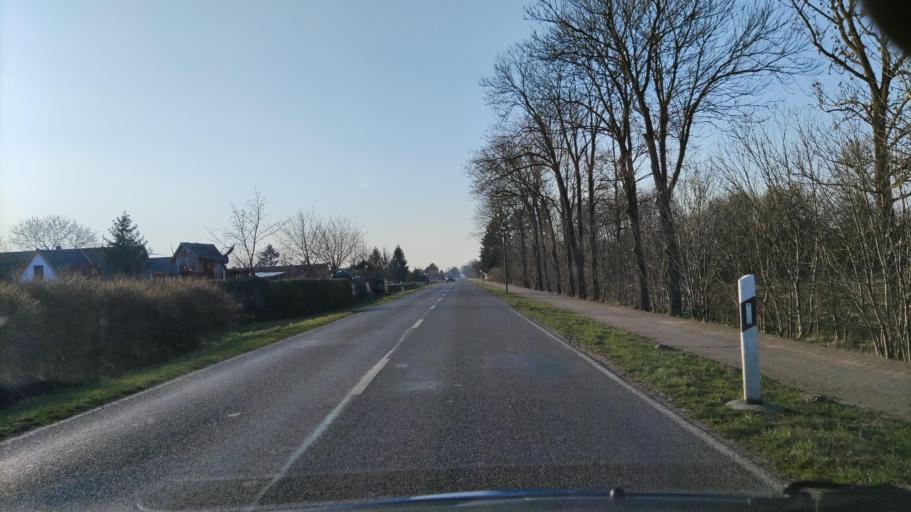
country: DE
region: Brandenburg
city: Cumlosen
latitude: 52.9528
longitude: 11.6491
